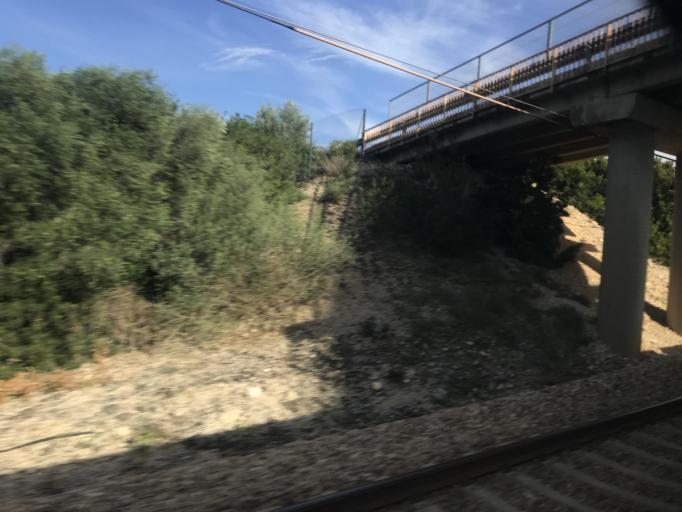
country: ES
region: Catalonia
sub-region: Provincia de Tarragona
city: Alcanar
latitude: 40.5465
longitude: 0.4306
